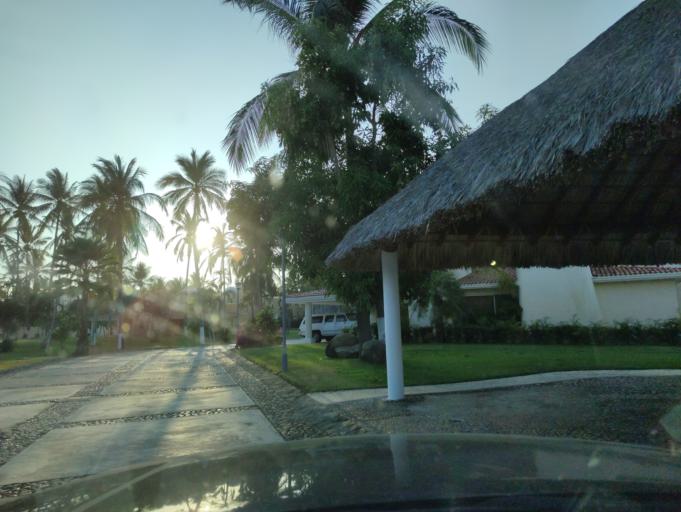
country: MX
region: Guerrero
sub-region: Acapulco de Juarez
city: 10 de Abril
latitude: 16.7703
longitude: -99.7813
